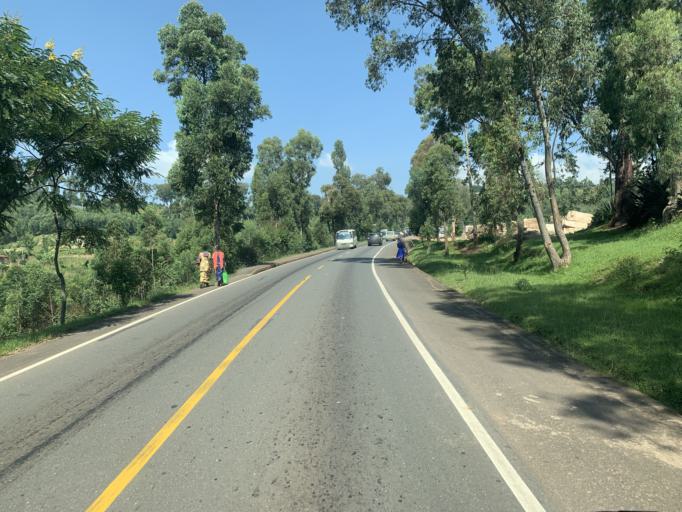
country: RW
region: Kigali
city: Kigali
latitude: -1.9927
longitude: 29.9213
